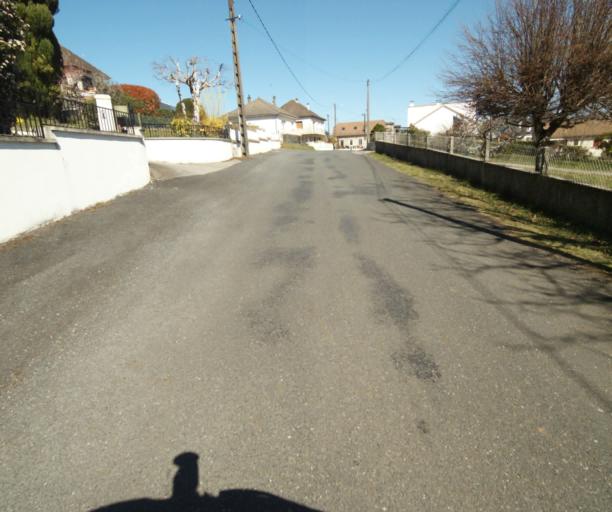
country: FR
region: Limousin
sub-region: Departement de la Correze
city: Seilhac
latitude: 45.3642
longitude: 1.7188
